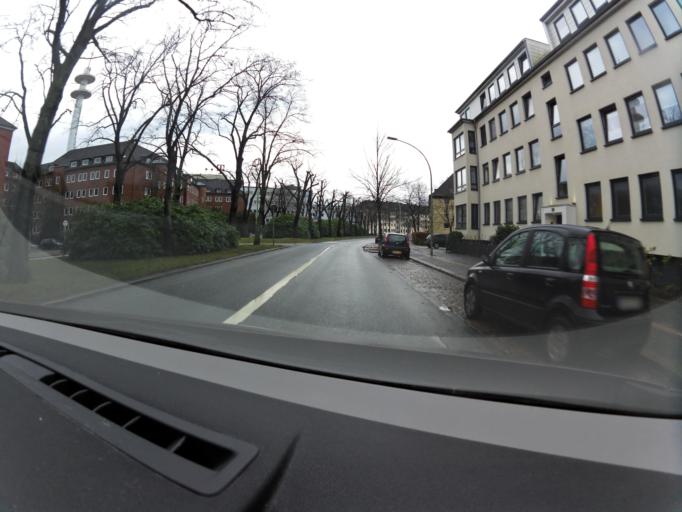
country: DE
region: Bremen
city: Bremerhaven
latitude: 53.5389
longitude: 8.5945
